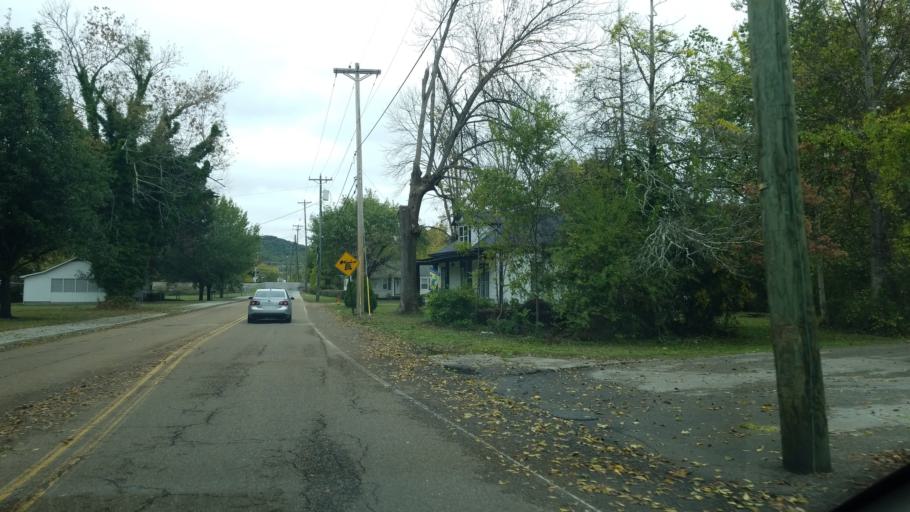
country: US
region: Tennessee
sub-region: Rhea County
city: Dayton
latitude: 35.4876
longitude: -85.0195
